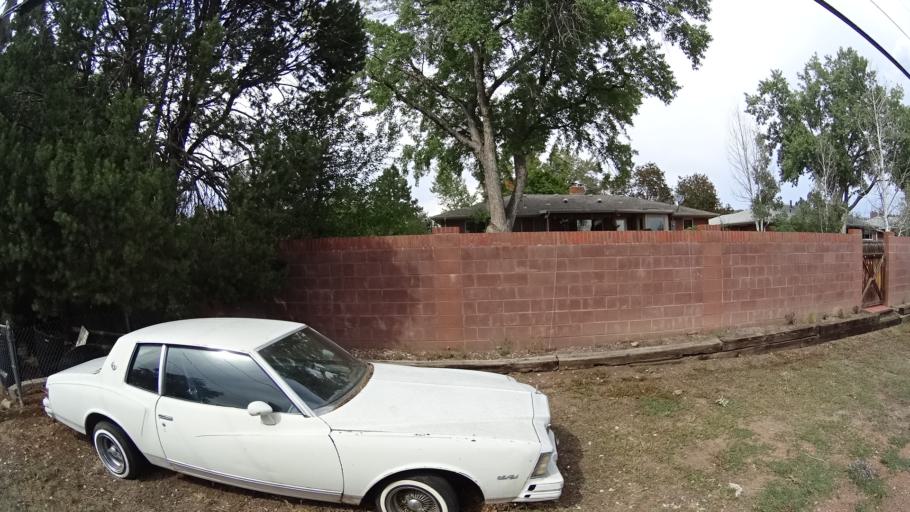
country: US
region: Colorado
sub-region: El Paso County
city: Colorado Springs
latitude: 38.8652
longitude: -104.7789
